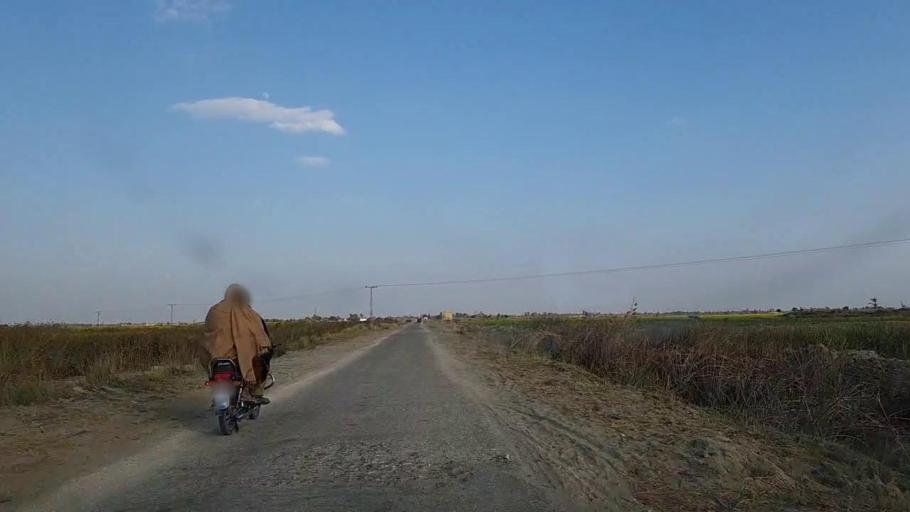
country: PK
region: Sindh
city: Sanghar
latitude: 26.2644
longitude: 68.9441
